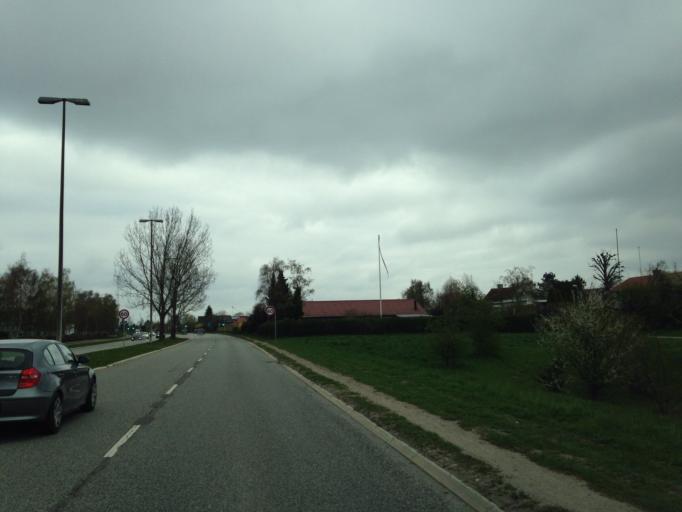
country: DK
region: Zealand
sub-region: Greve Kommune
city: Greve
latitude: 55.5905
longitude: 12.3021
